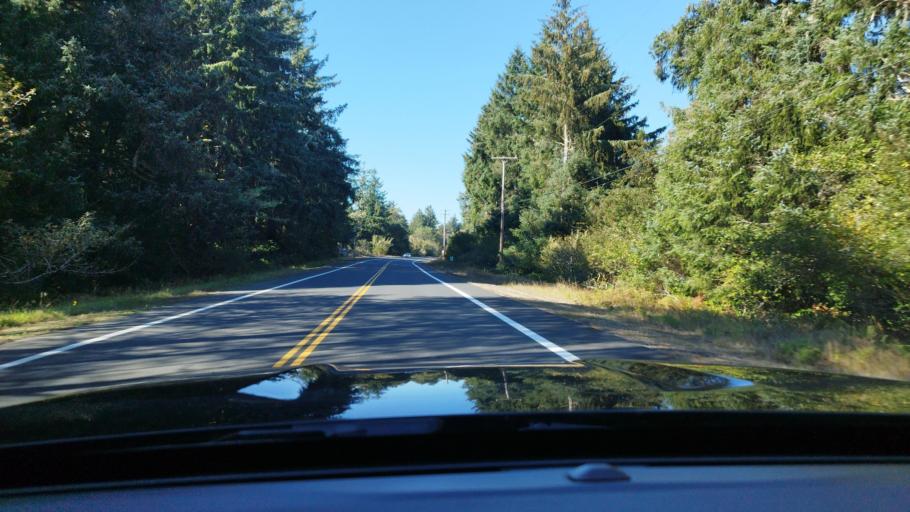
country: US
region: Oregon
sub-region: Clatsop County
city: Warrenton
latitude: 46.1737
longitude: -123.9509
